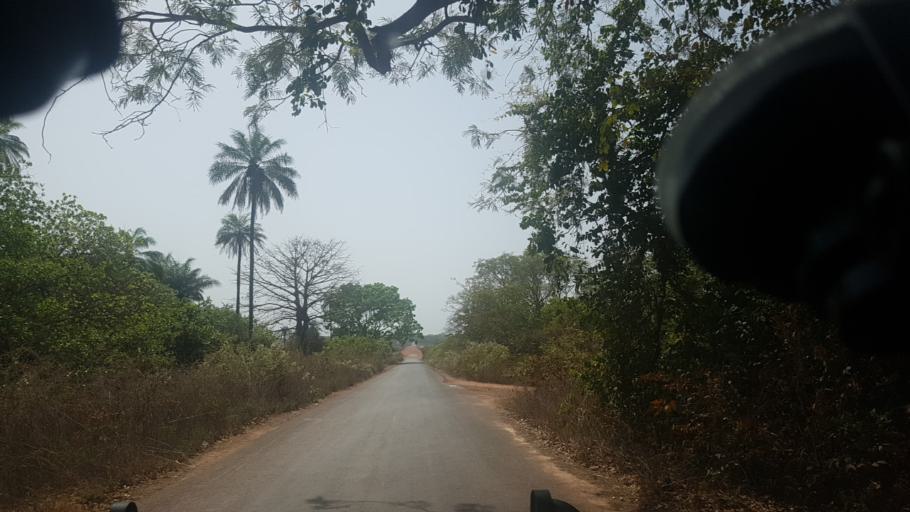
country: GW
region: Cacheu
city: Cacheu
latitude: 12.4128
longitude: -16.0771
